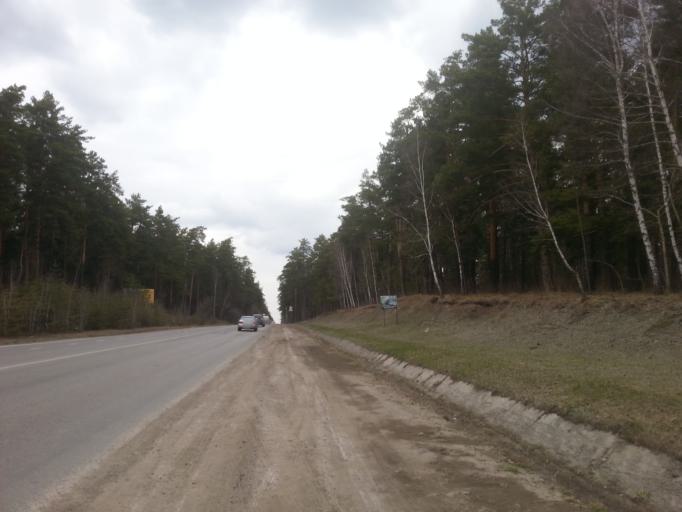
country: RU
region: Altai Krai
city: Yuzhnyy
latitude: 53.2703
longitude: 83.7249
